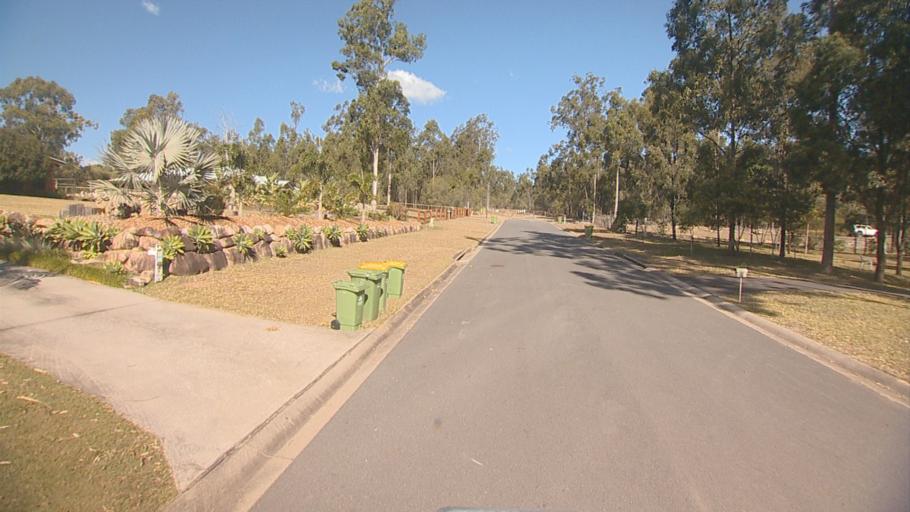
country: AU
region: Queensland
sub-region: Logan
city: North Maclean
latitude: -27.7546
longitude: 152.9405
